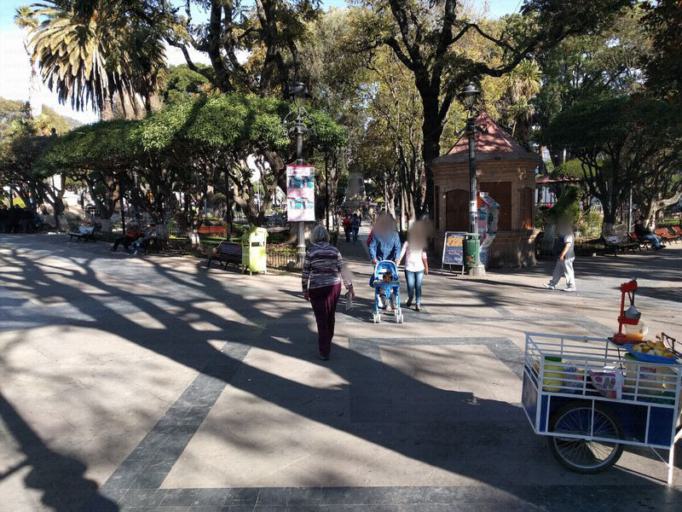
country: BO
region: Chuquisaca
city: Sucre
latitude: -19.0474
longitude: -65.2596
